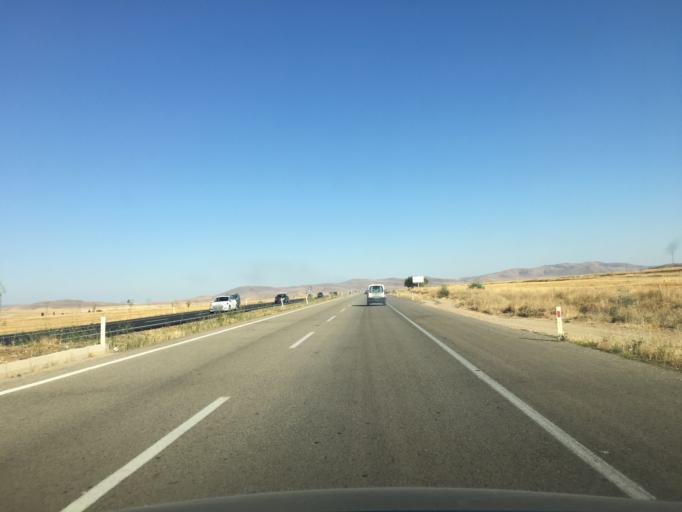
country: TR
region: Kirsehir
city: Akpinar
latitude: 39.3275
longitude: 34.0415
